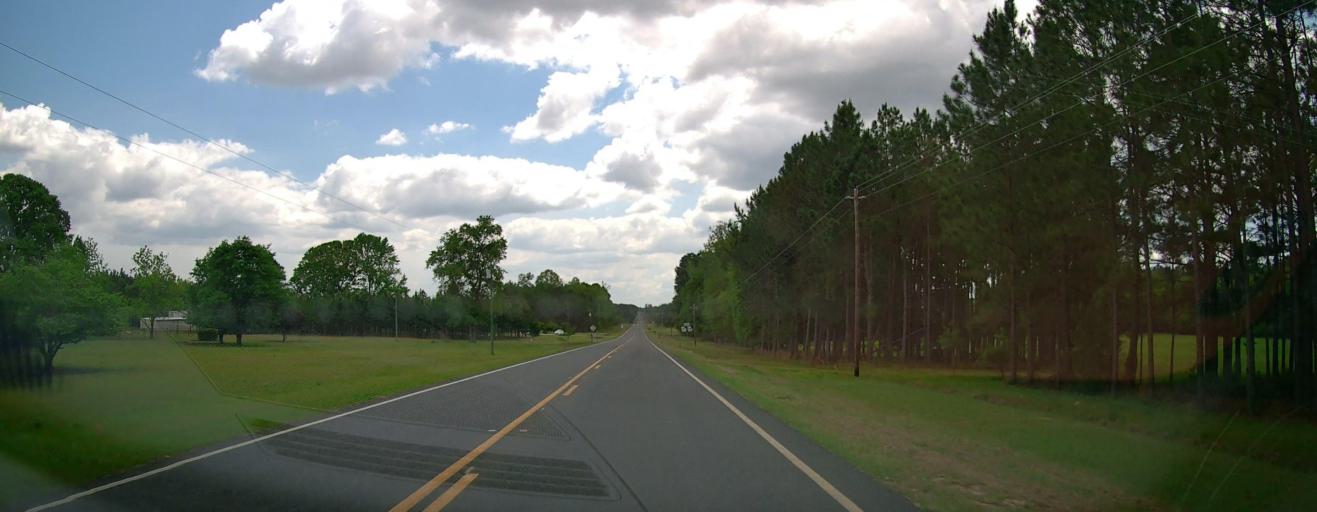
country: US
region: Georgia
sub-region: Treutlen County
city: Soperton
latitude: 32.4623
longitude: -82.6034
